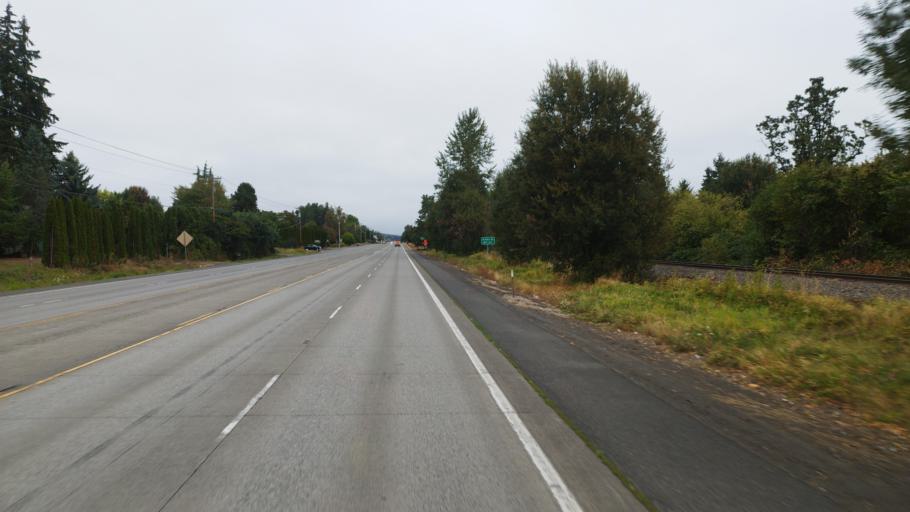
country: US
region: Oregon
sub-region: Columbia County
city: Warren
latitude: 45.8291
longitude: -122.8428
